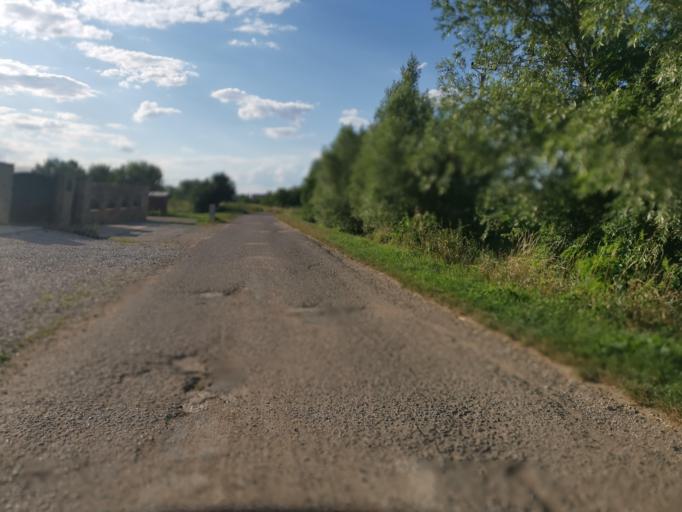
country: SK
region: Trnavsky
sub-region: Okres Skalica
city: Skalica
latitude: 48.8383
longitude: 17.2474
